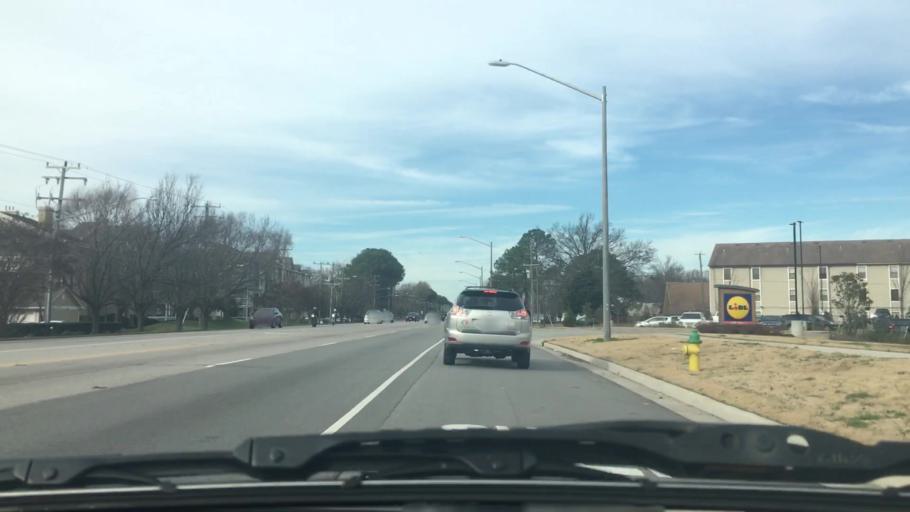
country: US
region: Virginia
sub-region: City of Norfolk
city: Norfolk
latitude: 36.8994
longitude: -76.2268
